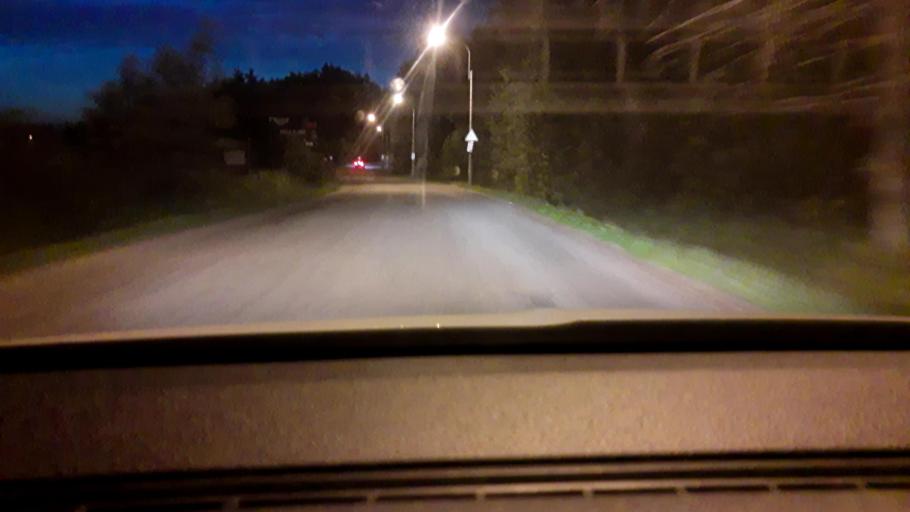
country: RU
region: Moskovskaya
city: Pavlovskaya Sloboda
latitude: 55.7818
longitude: 37.0760
